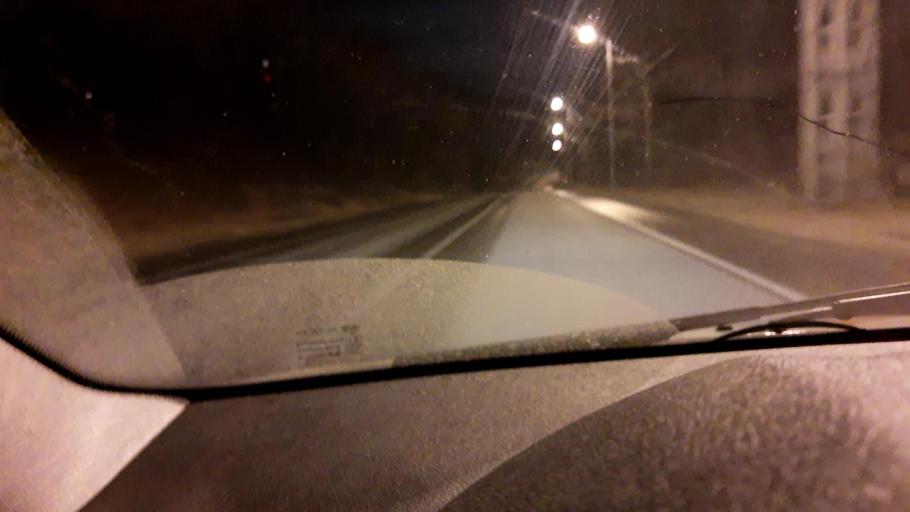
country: RU
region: Bashkortostan
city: Ufa
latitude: 54.8800
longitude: 56.0608
